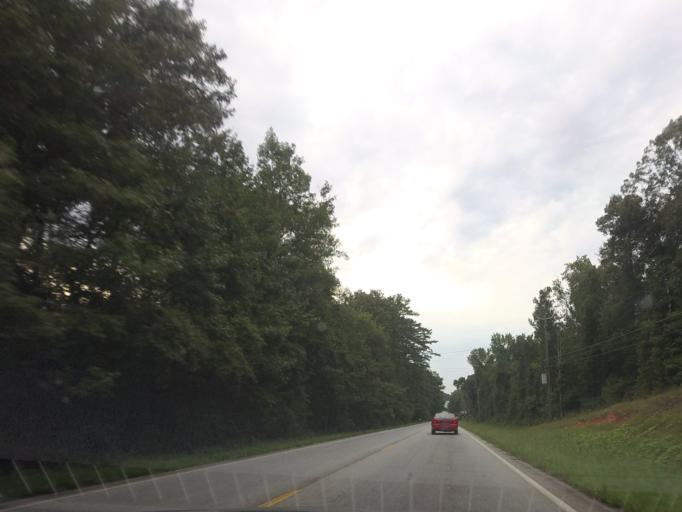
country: US
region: Georgia
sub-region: Bibb County
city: Macon
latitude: 32.8172
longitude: -83.5221
